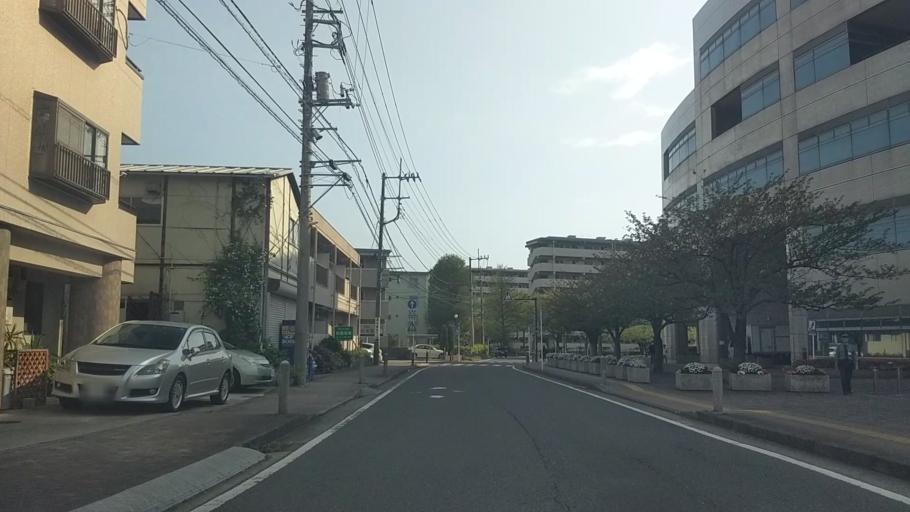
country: JP
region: Kanagawa
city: Kamakura
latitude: 35.3683
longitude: 139.5542
